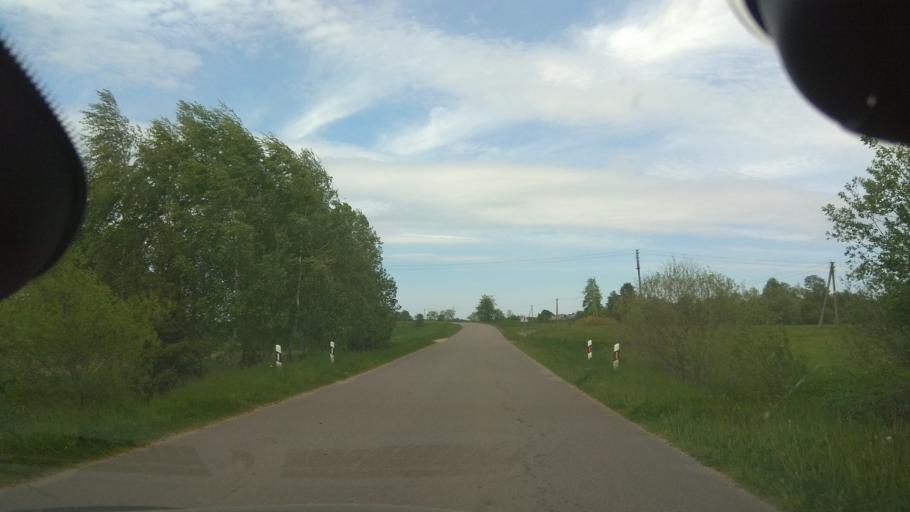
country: LT
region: Vilnius County
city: Ukmerge
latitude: 55.1009
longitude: 24.6972
